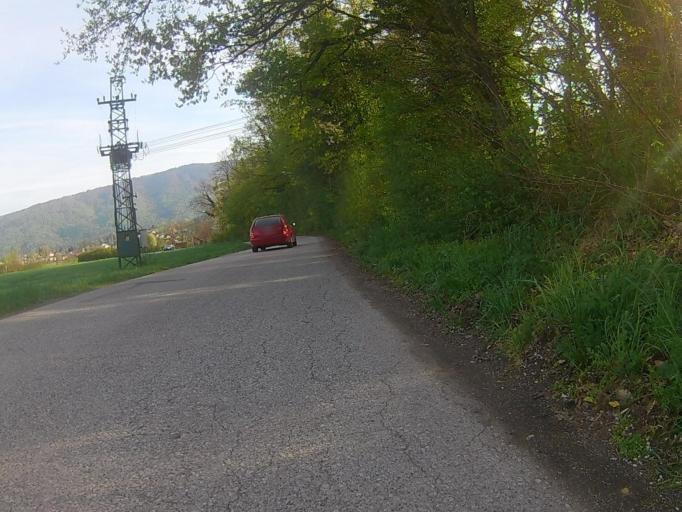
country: SI
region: Maribor
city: Limbus
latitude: 46.5604
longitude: 15.5857
